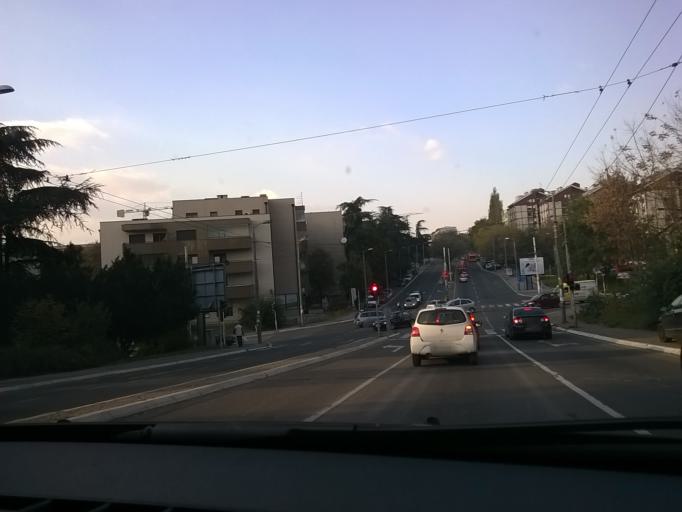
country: RS
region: Central Serbia
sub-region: Belgrade
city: Vozdovac
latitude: 44.7859
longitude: 20.5005
